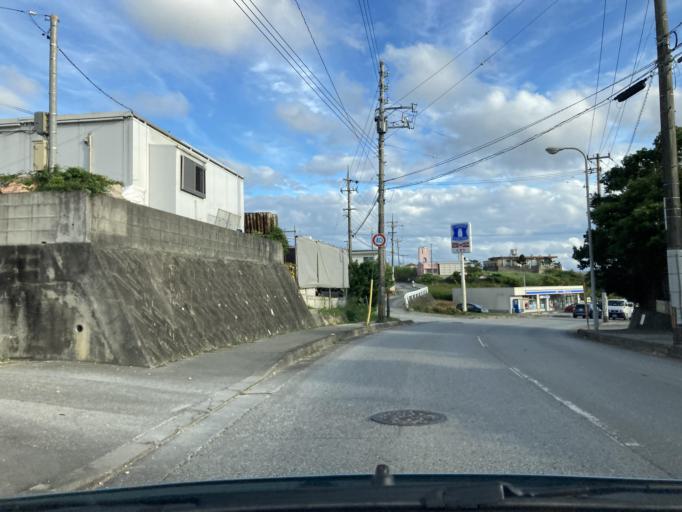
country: JP
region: Okinawa
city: Tomigusuku
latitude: 26.1465
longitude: 127.7447
